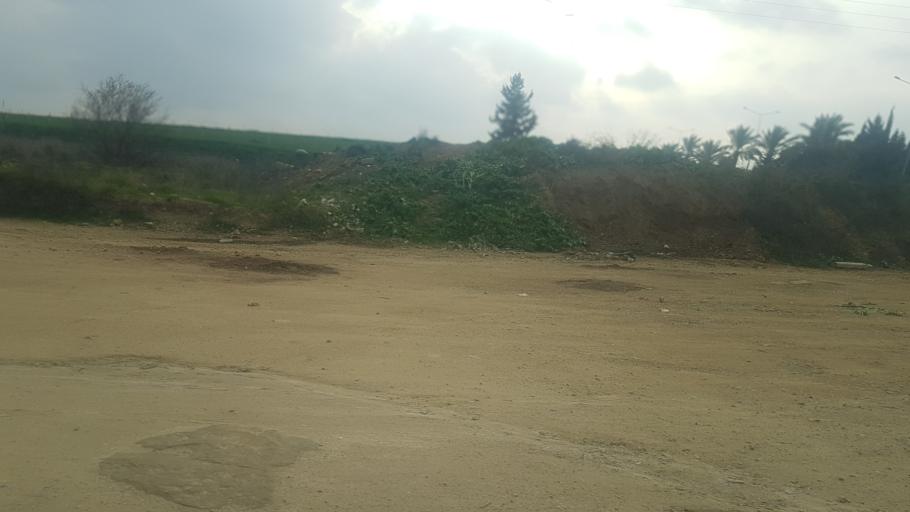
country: TR
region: Adana
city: Seyhan
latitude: 37.0514
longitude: 35.2085
